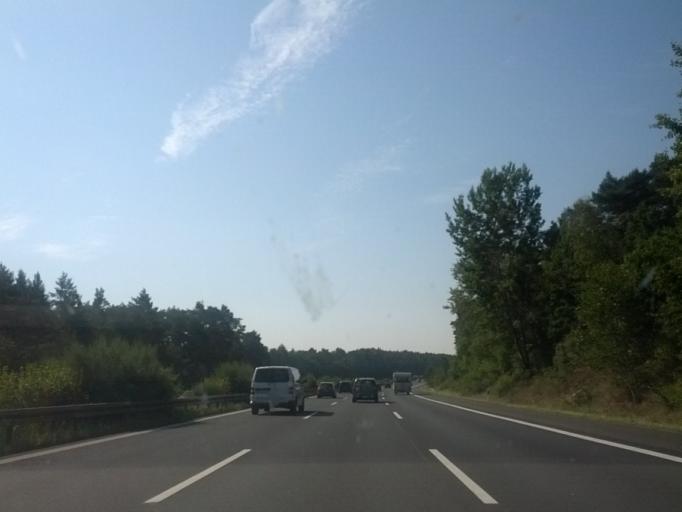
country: DE
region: Brandenburg
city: Beelitz
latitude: 52.2352
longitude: 12.9172
